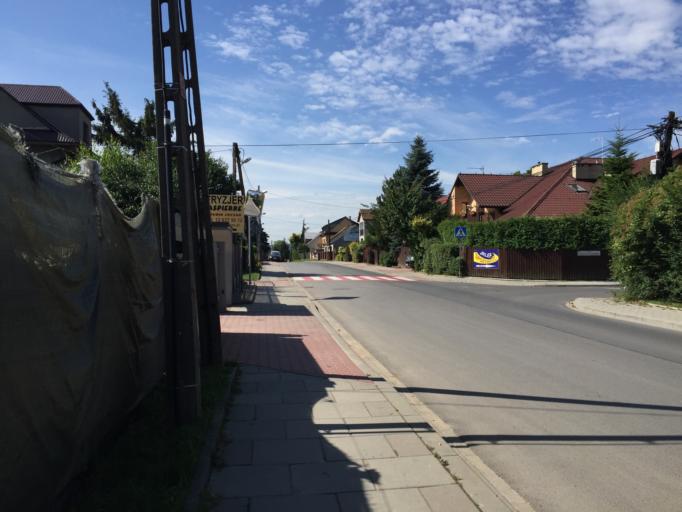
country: PL
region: Lesser Poland Voivodeship
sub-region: Powiat krakowski
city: Rzaska
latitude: 50.0883
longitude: 19.8823
